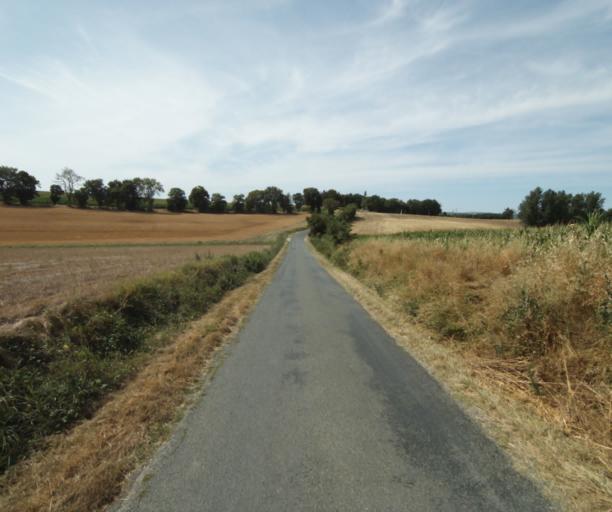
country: FR
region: Midi-Pyrenees
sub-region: Departement du Tarn
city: Soreze
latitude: 43.4976
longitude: 2.0488
